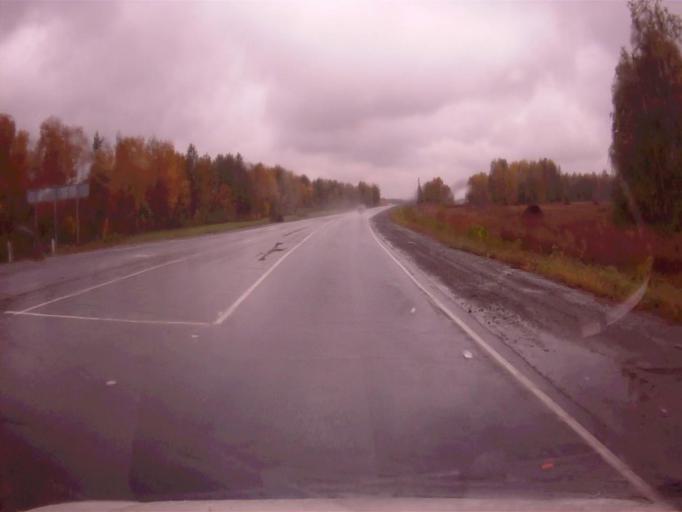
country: RU
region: Chelyabinsk
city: Roshchino
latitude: 55.4001
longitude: 61.0745
